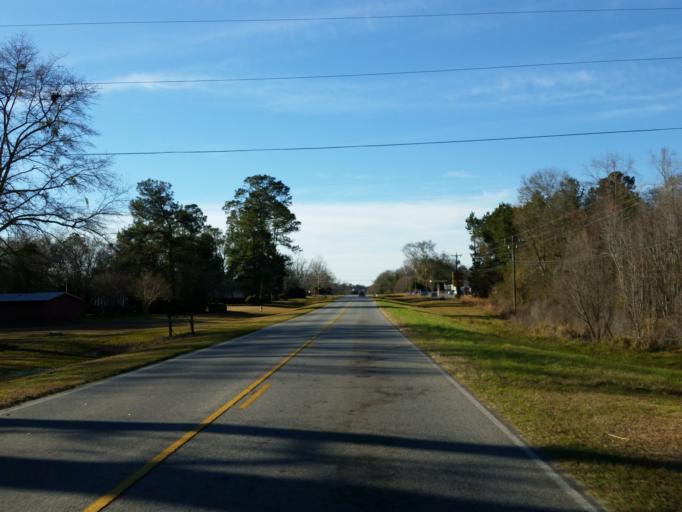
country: US
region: Georgia
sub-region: Lowndes County
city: Remerton
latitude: 30.9023
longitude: -83.3370
